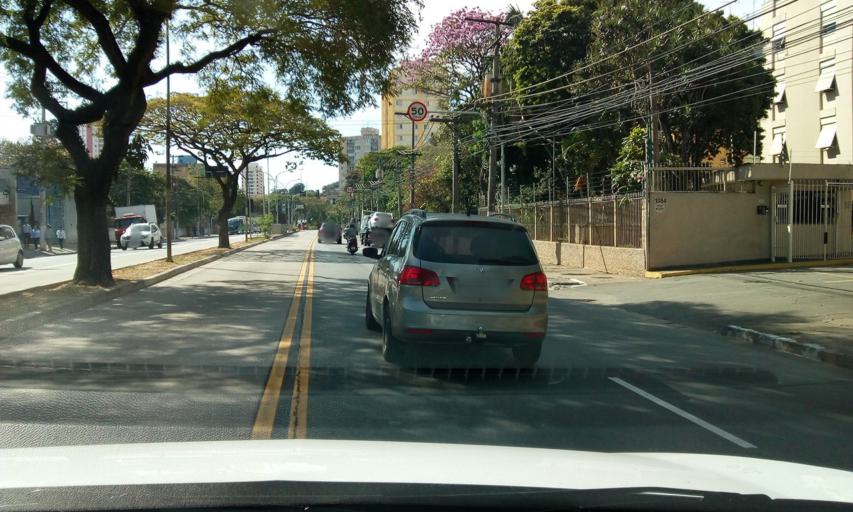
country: BR
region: Sao Paulo
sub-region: Sao Paulo
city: Sao Paulo
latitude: -23.5115
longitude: -46.6662
